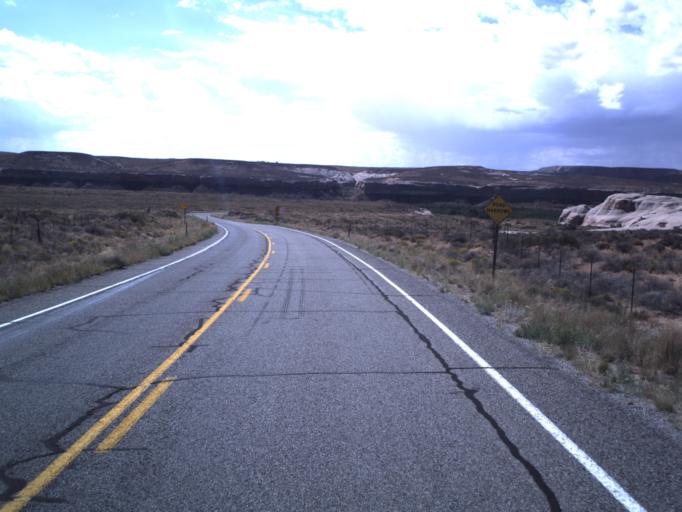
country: US
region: Utah
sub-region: San Juan County
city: Blanding
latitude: 37.2906
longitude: -109.4896
